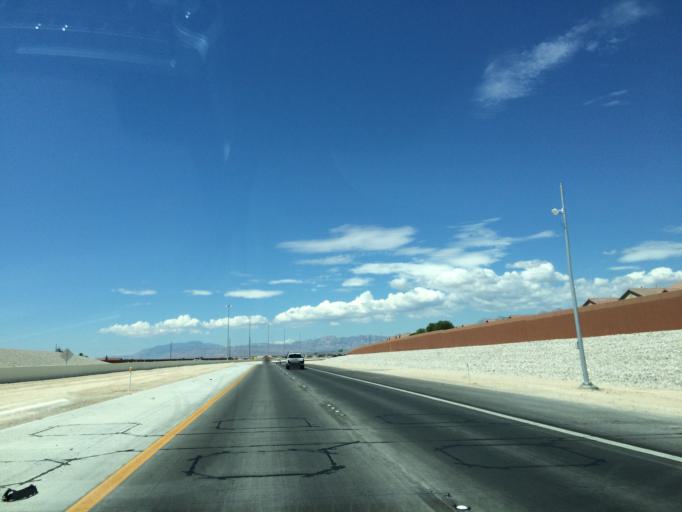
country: US
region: Nevada
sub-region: Clark County
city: North Las Vegas
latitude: 36.2804
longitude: -115.1924
